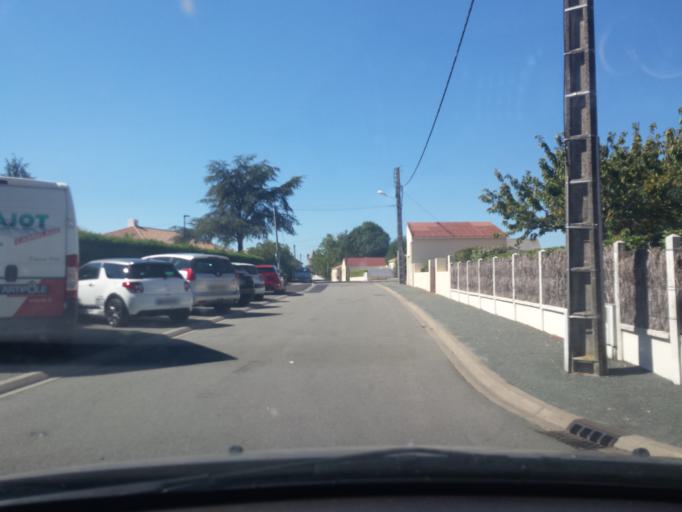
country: FR
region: Pays de la Loire
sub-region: Departement de la Vendee
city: Apremont
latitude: 46.7484
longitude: -1.7364
